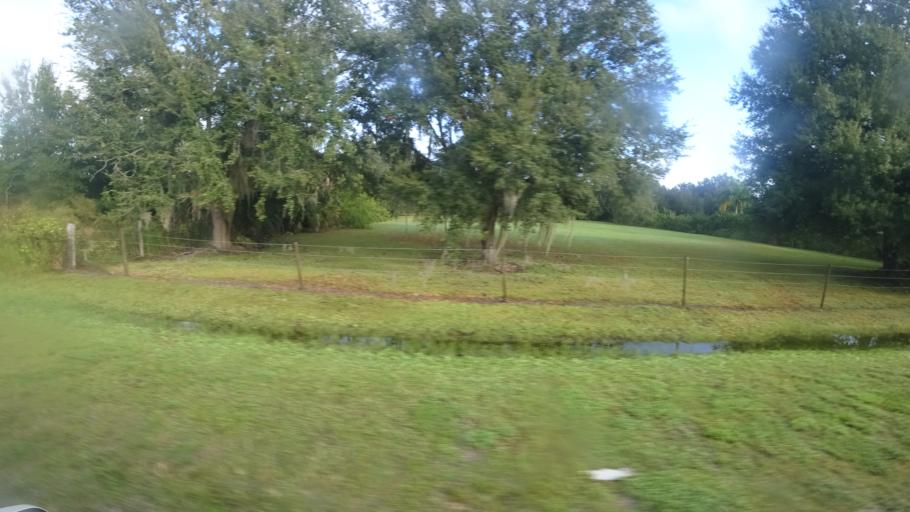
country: US
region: Florida
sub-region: Manatee County
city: Ellenton
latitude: 27.5354
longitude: -82.4730
